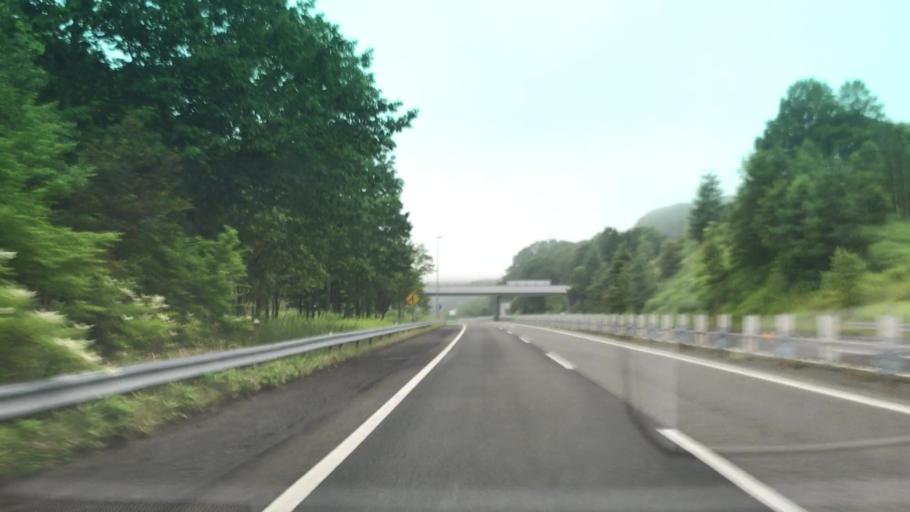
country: JP
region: Hokkaido
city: Shiraoi
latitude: 42.4625
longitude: 141.1756
